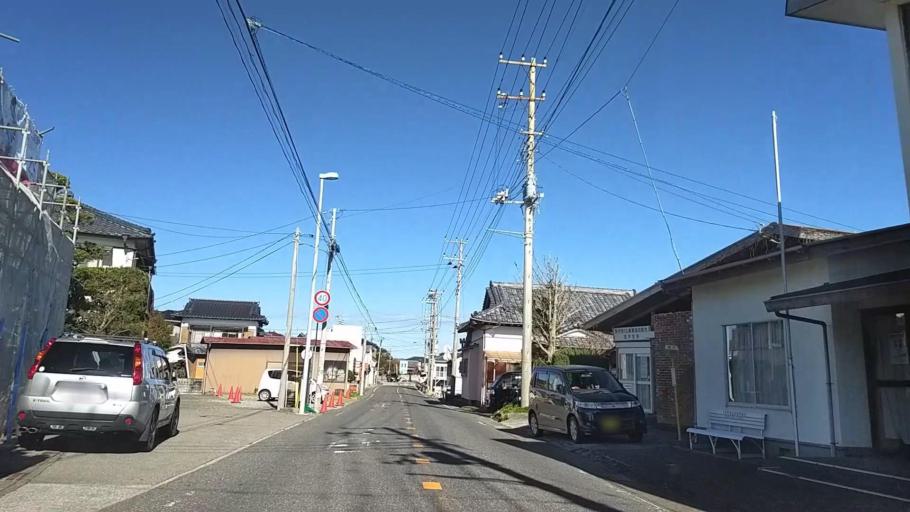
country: JP
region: Chiba
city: Tateyama
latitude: 34.9471
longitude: 139.9629
